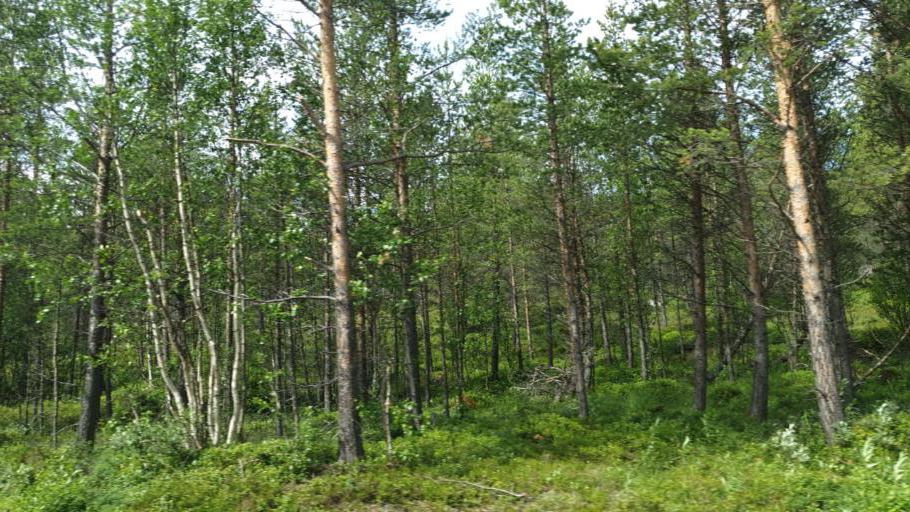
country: NO
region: Oppland
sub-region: Vaga
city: Vagamo
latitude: 61.6841
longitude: 9.0585
